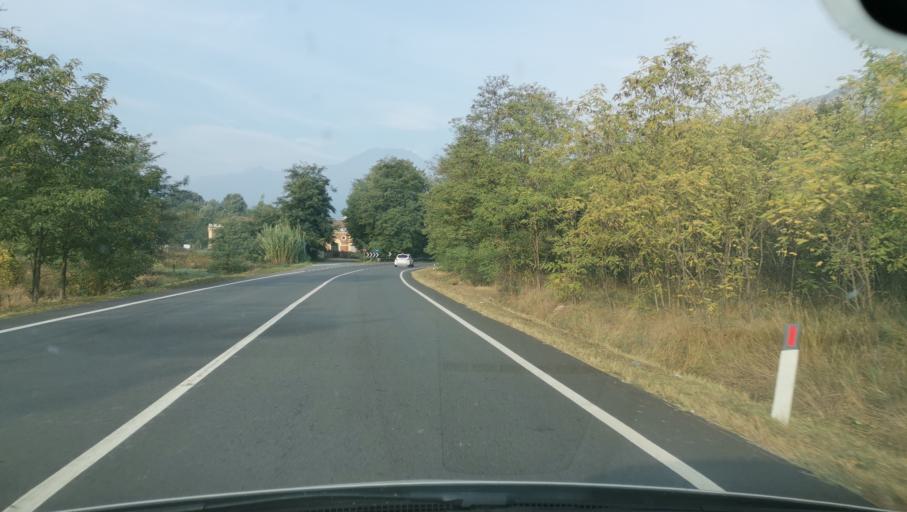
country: IT
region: Piedmont
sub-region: Provincia di Torino
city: Mattie
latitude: 45.1319
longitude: 7.1190
